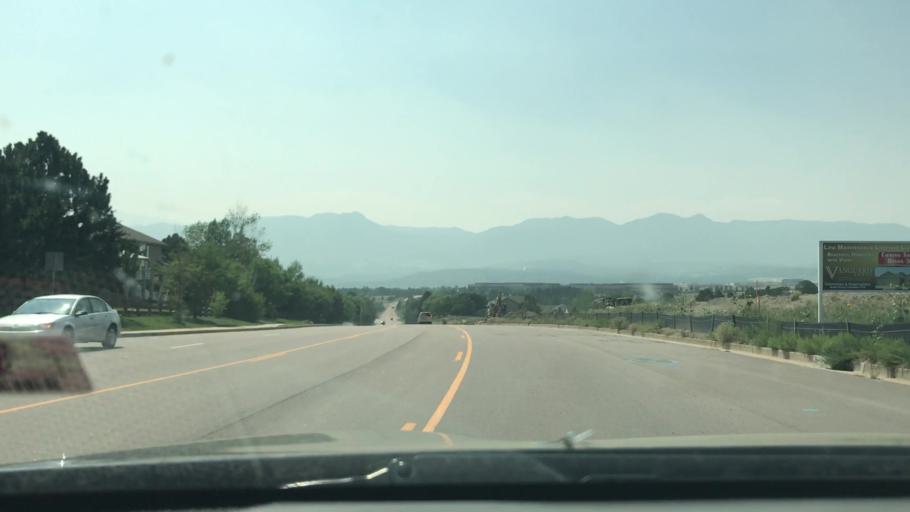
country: US
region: Colorado
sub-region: El Paso County
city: Gleneagle
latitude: 38.9823
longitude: -104.7757
